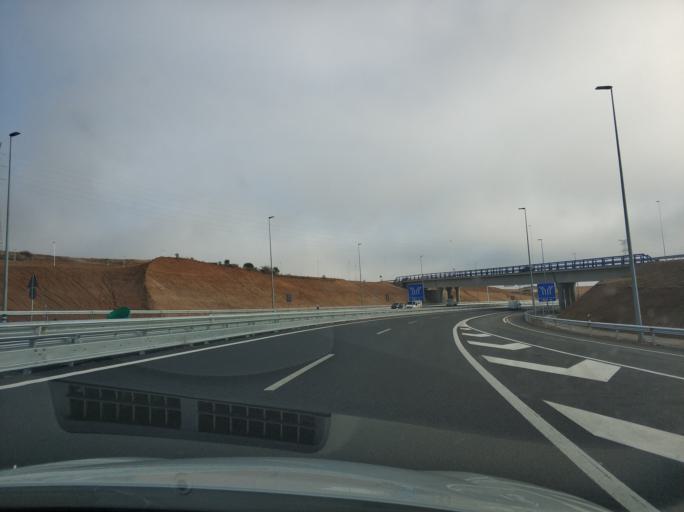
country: ES
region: Castille and Leon
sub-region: Provincia de Leon
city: Leon
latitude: 42.5766
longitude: -5.5412
